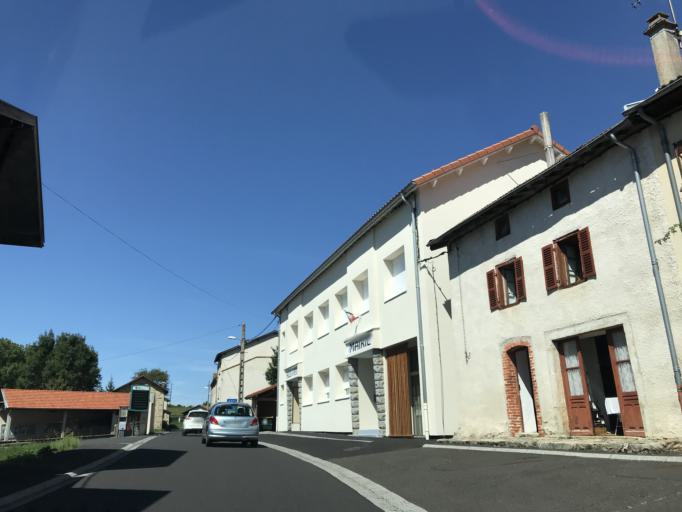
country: FR
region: Auvergne
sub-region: Departement du Puy-de-Dome
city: Job
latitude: 45.6747
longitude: 3.7428
